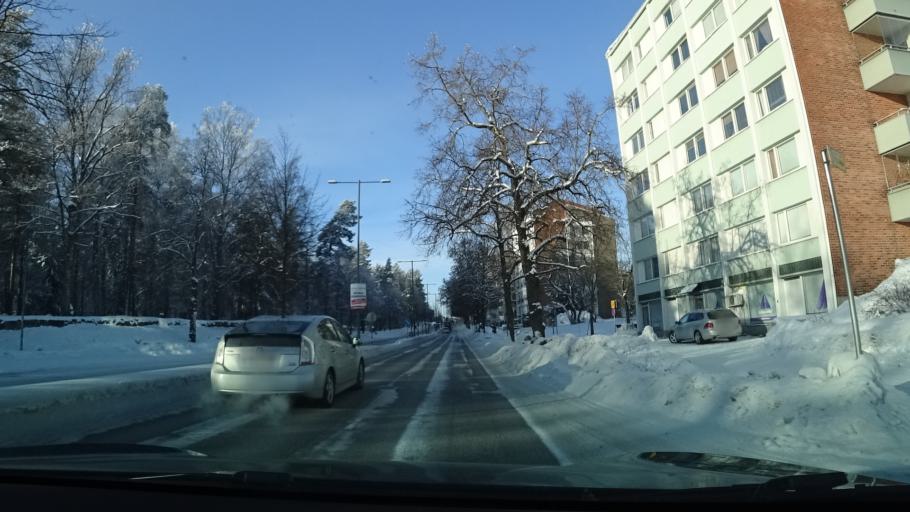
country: FI
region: South Karelia
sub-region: Lappeenranta
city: Lappeenranta
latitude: 61.0510
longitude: 28.1949
